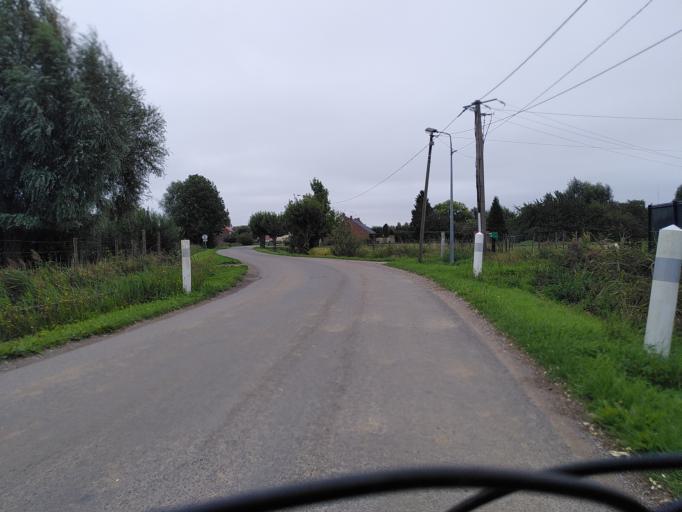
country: FR
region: Nord-Pas-de-Calais
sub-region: Departement du Pas-de-Calais
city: Saint-Venant
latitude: 50.6267
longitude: 2.5401
